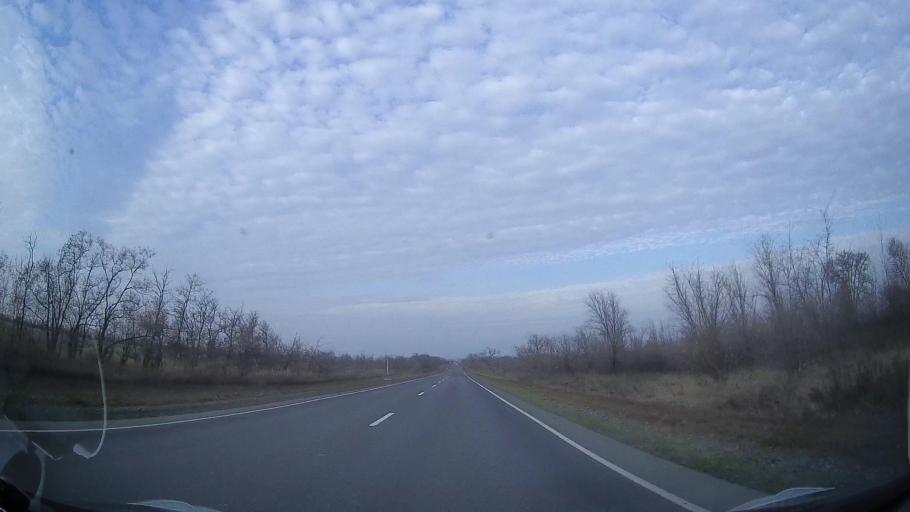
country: RU
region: Rostov
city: Bagayevskaya
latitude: 47.1491
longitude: 40.2765
